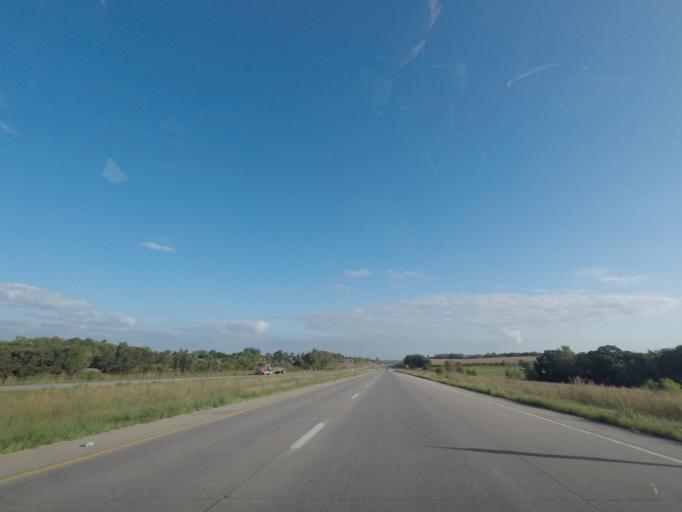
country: US
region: Iowa
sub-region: Warren County
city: Carlisle
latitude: 41.5262
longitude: -93.5193
